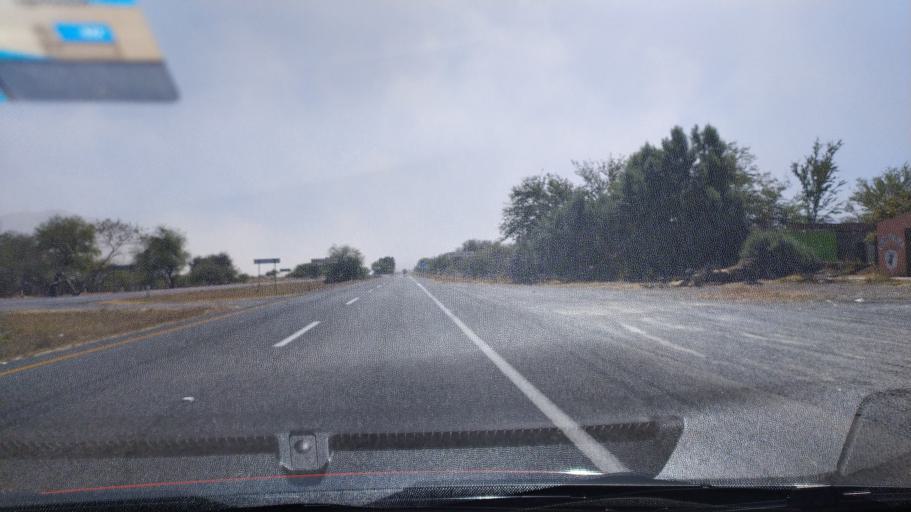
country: MX
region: Jalisco
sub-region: Acatlan de Juarez
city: Villa de los Ninos
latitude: 20.3334
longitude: -103.5697
